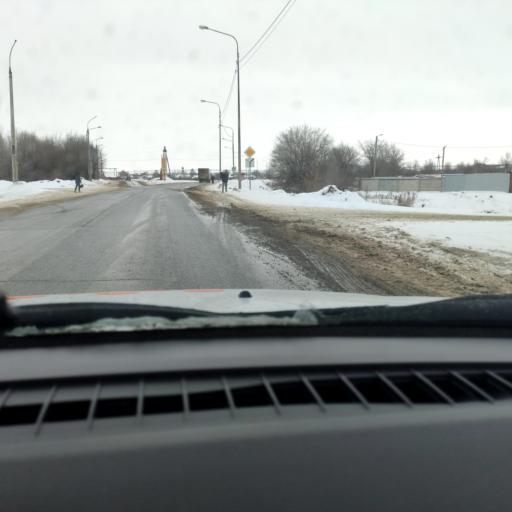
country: RU
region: Samara
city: Dubovyy Umet
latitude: 52.8265
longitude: 50.4996
